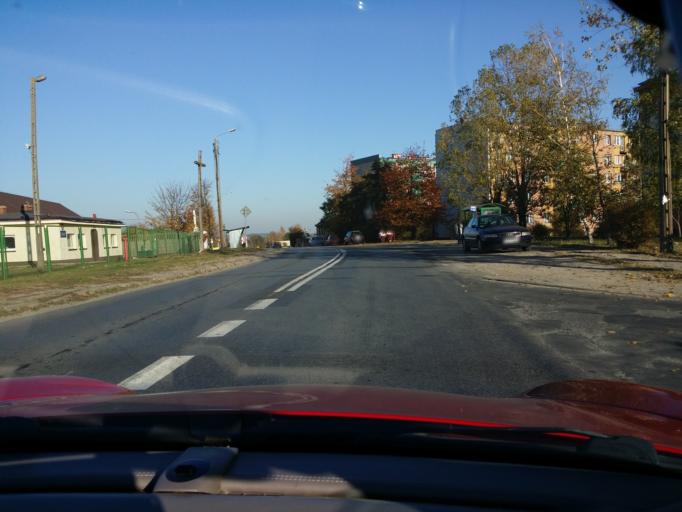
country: PL
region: Masovian Voivodeship
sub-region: Powiat radomski
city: Wierzbica
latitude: 51.2491
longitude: 21.0665
